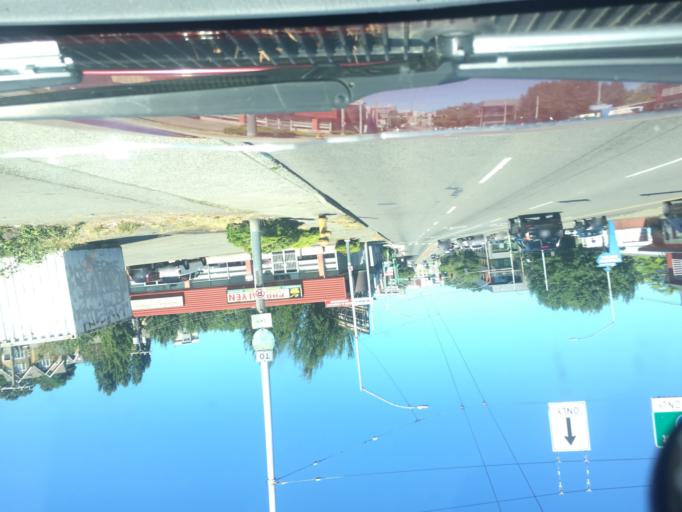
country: US
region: Washington
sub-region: King County
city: Seattle
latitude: 47.5949
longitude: -122.3107
